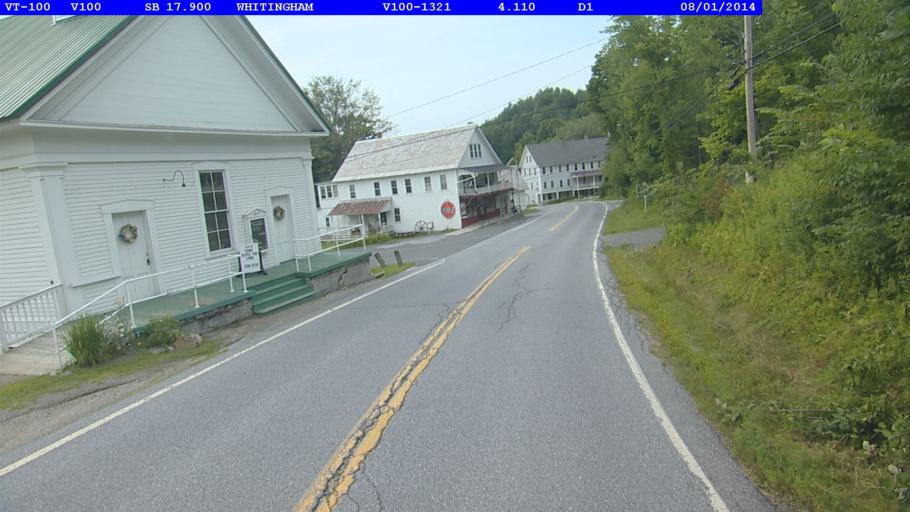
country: US
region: Massachusetts
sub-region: Franklin County
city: Charlemont
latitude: 42.7886
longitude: -72.8837
